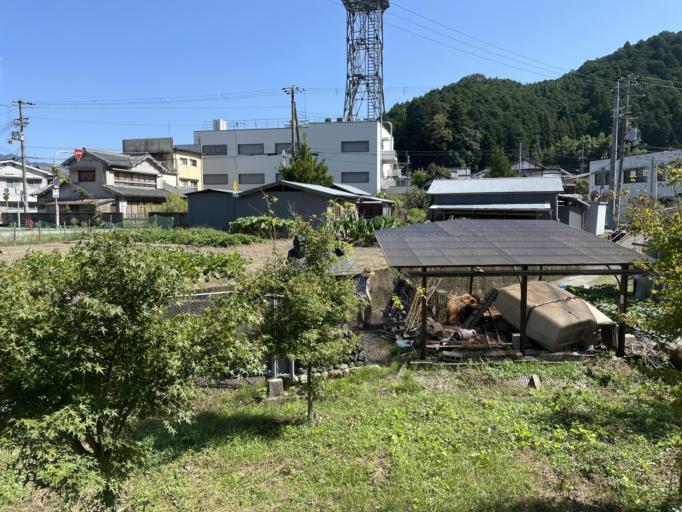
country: JP
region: Nara
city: Yoshino-cho
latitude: 34.3891
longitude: 135.8486
